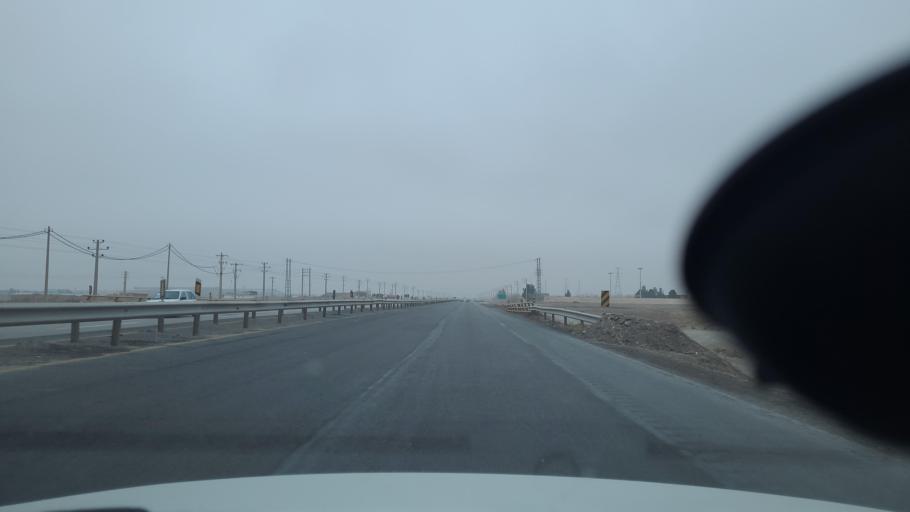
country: IR
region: Razavi Khorasan
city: Fariman
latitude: 35.9281
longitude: 59.7526
